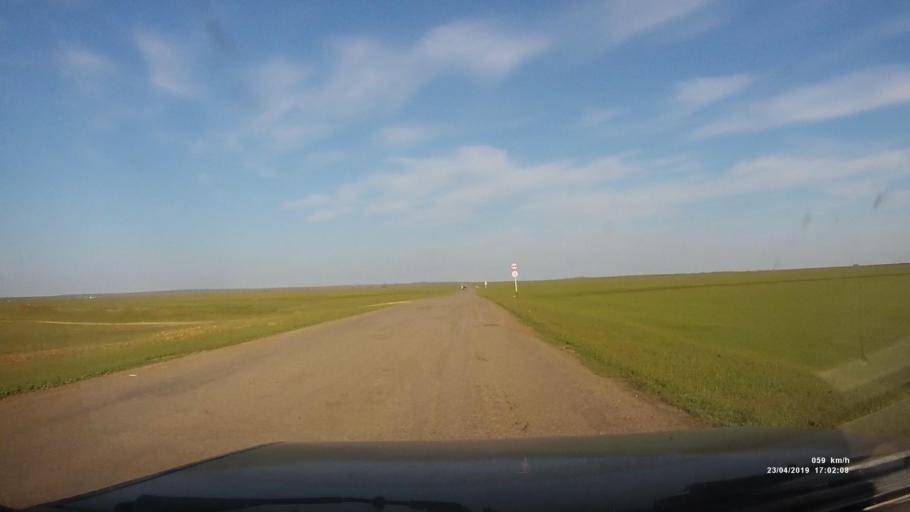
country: RU
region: Kalmykiya
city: Priyutnoye
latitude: 46.2935
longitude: 43.4139
